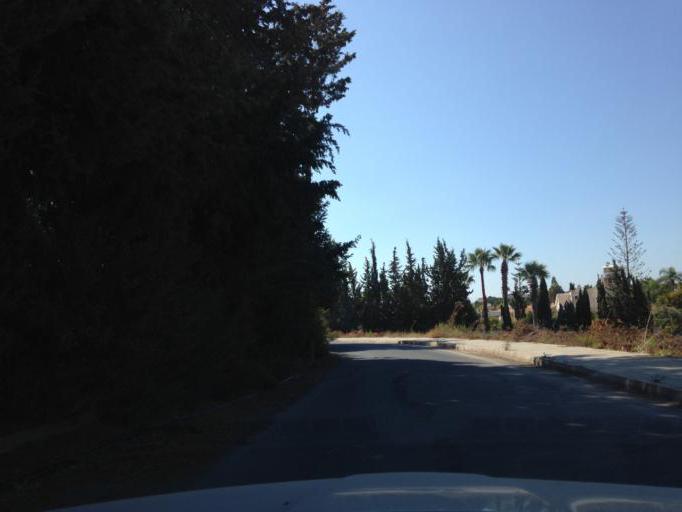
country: CY
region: Pafos
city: Pegeia
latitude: 34.8617
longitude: 32.3639
